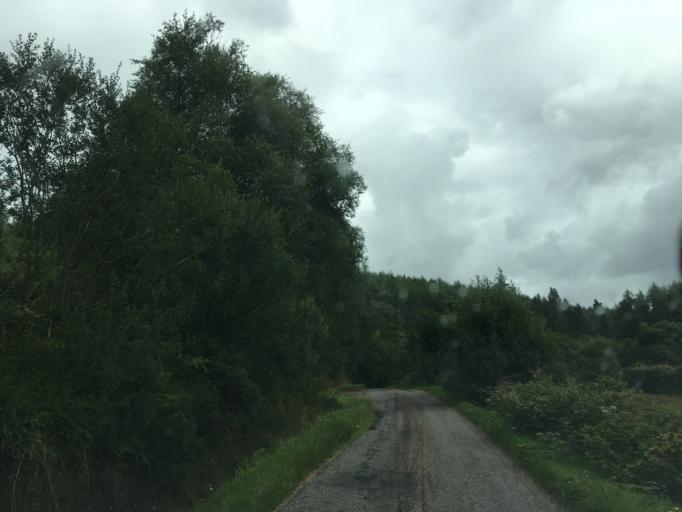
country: GB
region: Scotland
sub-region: Argyll and Bute
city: Oban
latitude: 56.2789
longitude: -5.3603
